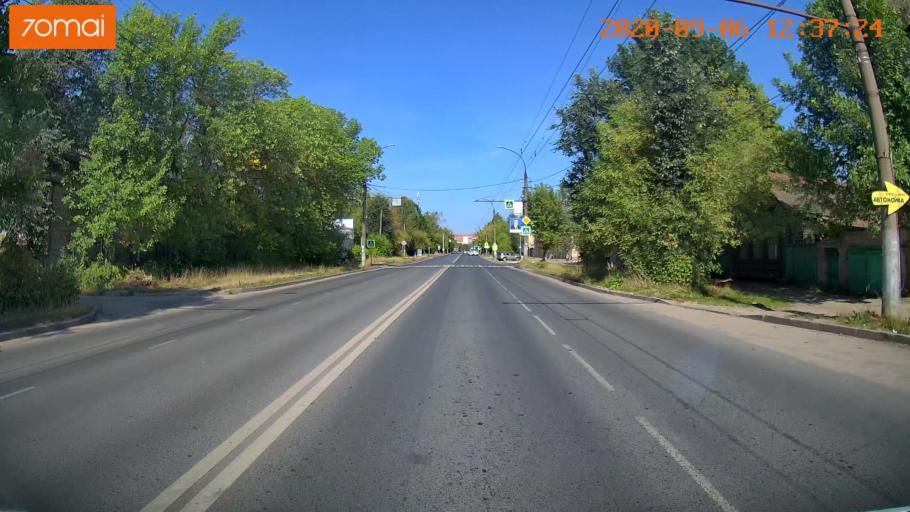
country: RU
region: Ivanovo
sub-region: Gorod Ivanovo
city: Ivanovo
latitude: 57.0265
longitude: 40.9798
